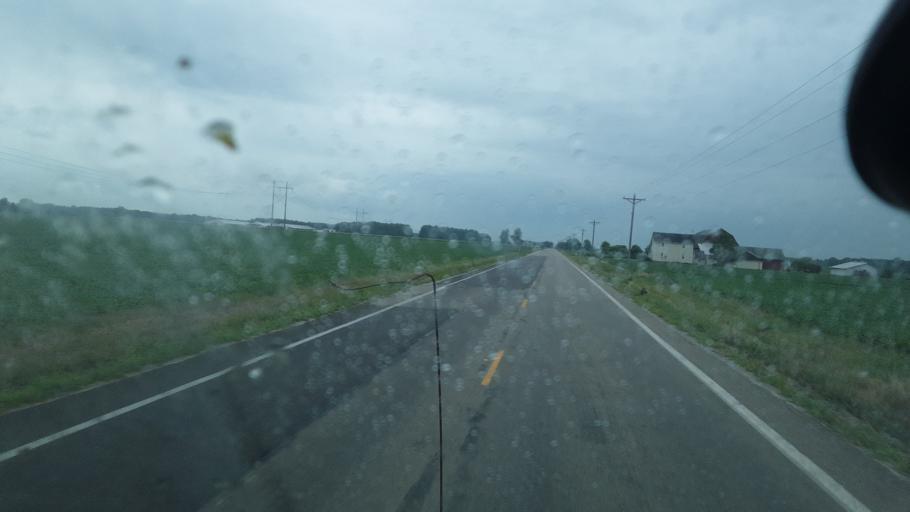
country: US
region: Ohio
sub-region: Defiance County
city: Hicksville
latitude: 41.2961
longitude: -84.6820
